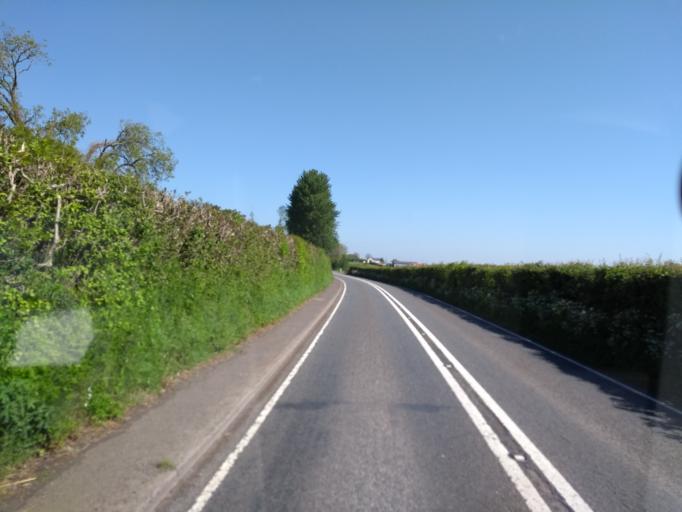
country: GB
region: England
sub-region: Somerset
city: Chard
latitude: 50.8525
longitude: -2.9568
